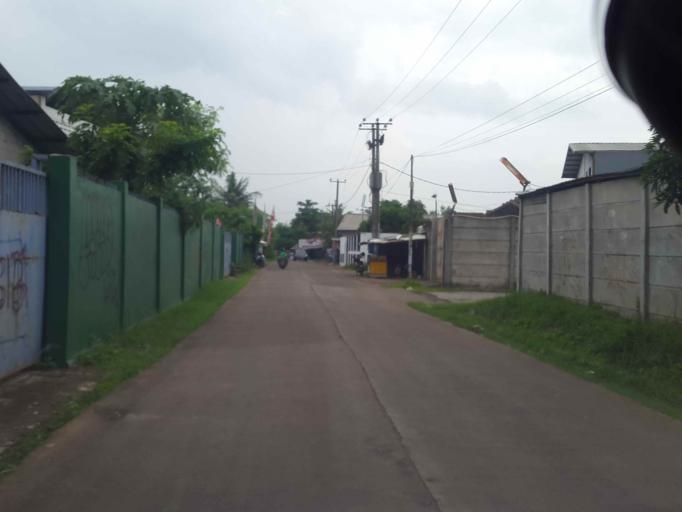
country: ID
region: West Java
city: Cikarang
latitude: -6.2946
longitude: 107.1812
